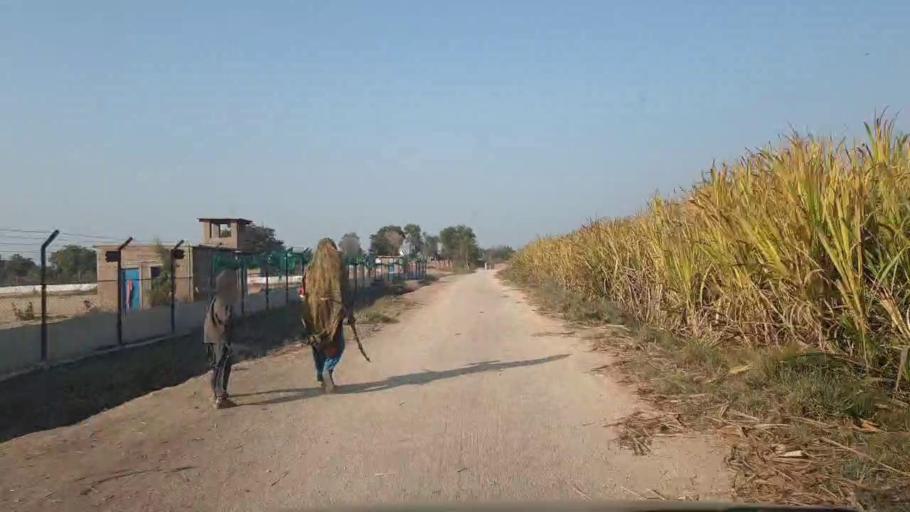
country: PK
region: Sindh
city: Bhit Shah
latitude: 25.8311
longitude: 68.5200
